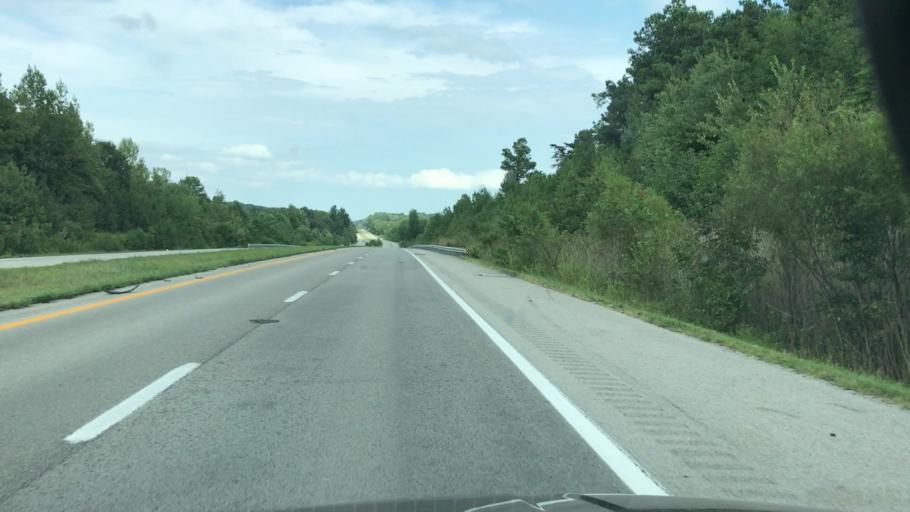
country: US
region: Kentucky
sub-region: Hopkins County
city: Earlington
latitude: 37.2022
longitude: -87.5259
